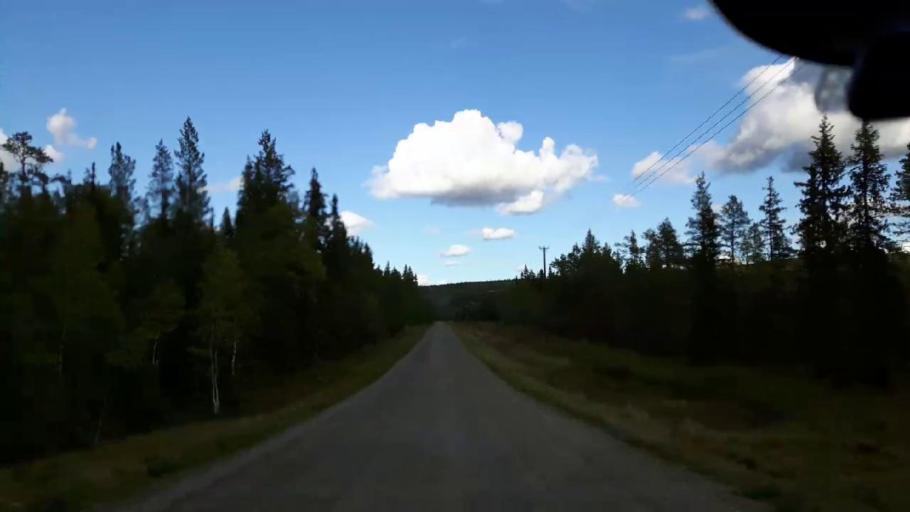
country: SE
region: Jaemtland
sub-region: Stroemsunds Kommun
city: Stroemsund
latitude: 63.4202
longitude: 15.7973
